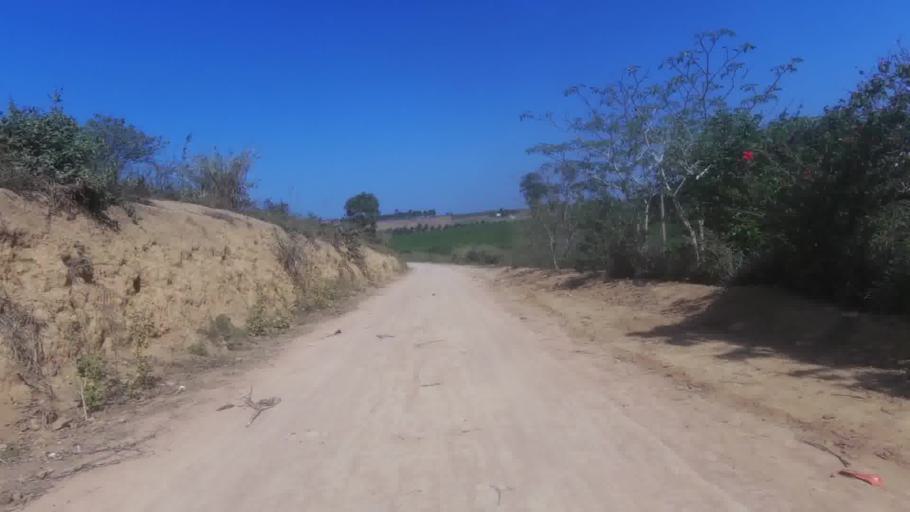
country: BR
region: Espirito Santo
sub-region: Marataizes
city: Marataizes
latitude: -21.1031
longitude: -40.8529
